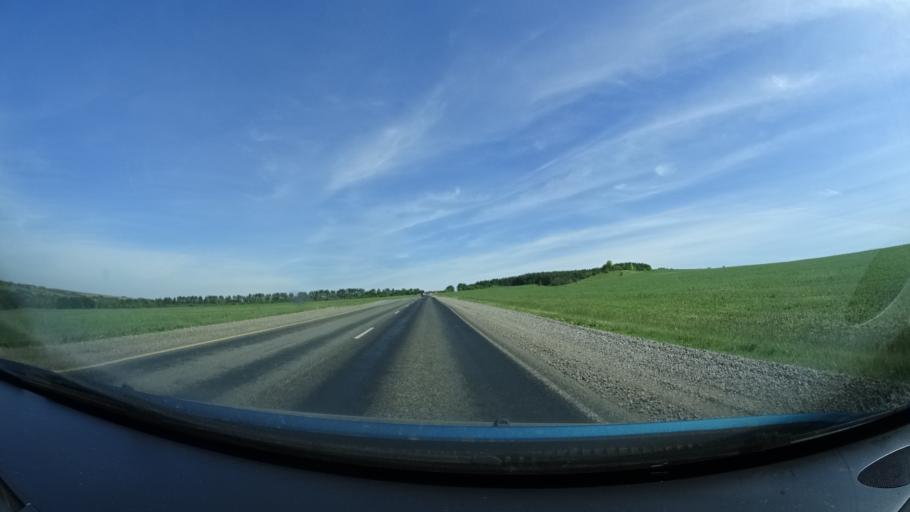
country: RU
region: Bashkortostan
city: Blagoveshchensk
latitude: 55.1271
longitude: 55.8428
